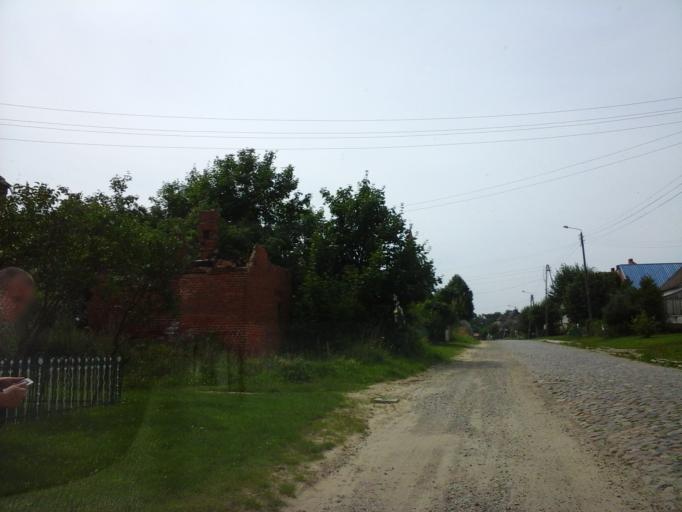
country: PL
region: West Pomeranian Voivodeship
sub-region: Powiat choszczenski
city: Bierzwnik
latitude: 52.9923
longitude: 15.6326
